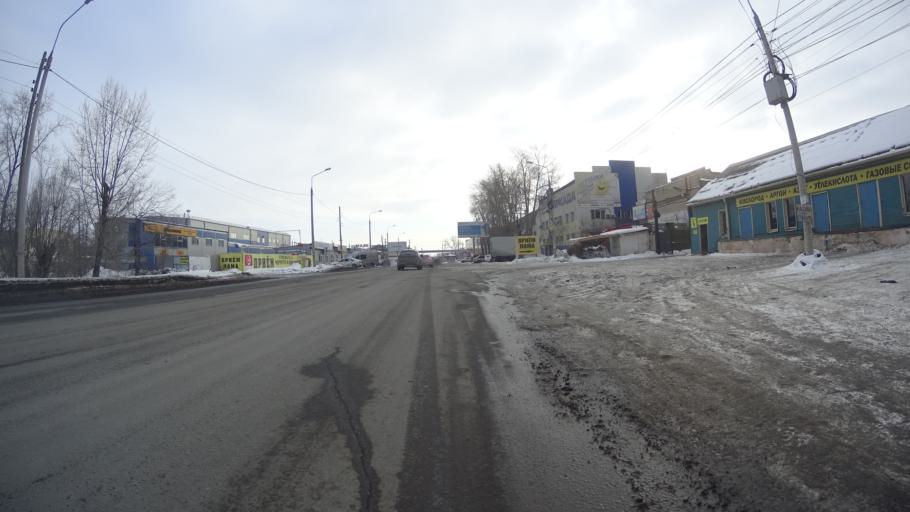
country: RU
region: Chelyabinsk
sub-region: Gorod Chelyabinsk
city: Chelyabinsk
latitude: 55.1223
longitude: 61.3859
